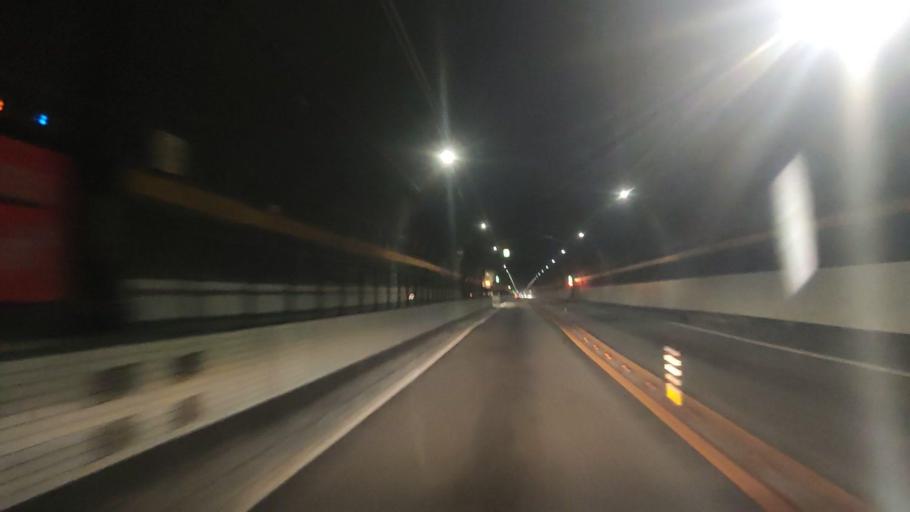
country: JP
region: Nagasaki
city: Obita
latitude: 32.7822
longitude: 129.8850
